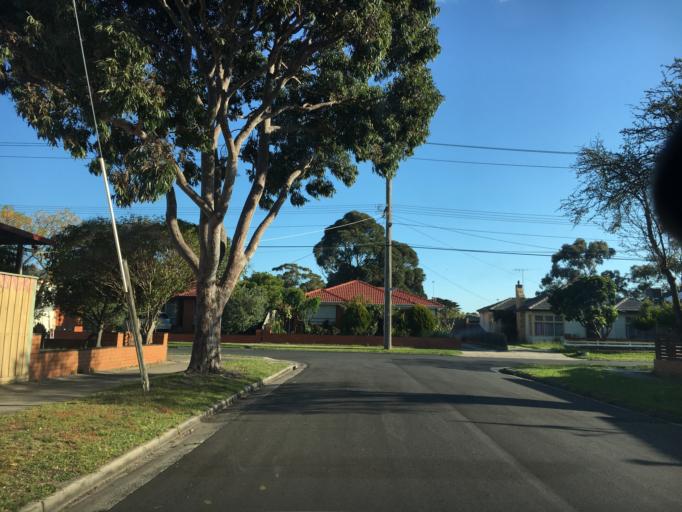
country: AU
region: Victoria
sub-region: Kingston
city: Clayton South
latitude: -37.9346
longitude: 145.1261
